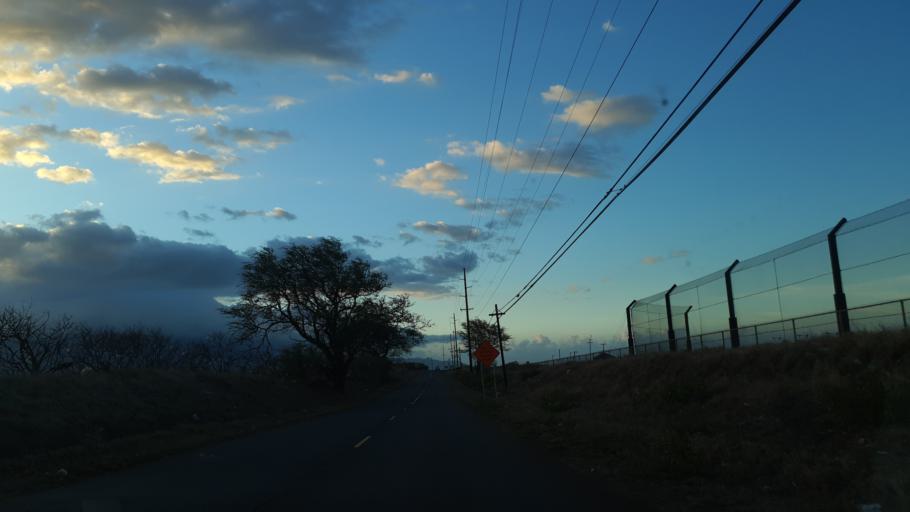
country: US
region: Hawaii
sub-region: Maui County
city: Kahului
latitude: 20.8566
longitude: -156.4229
